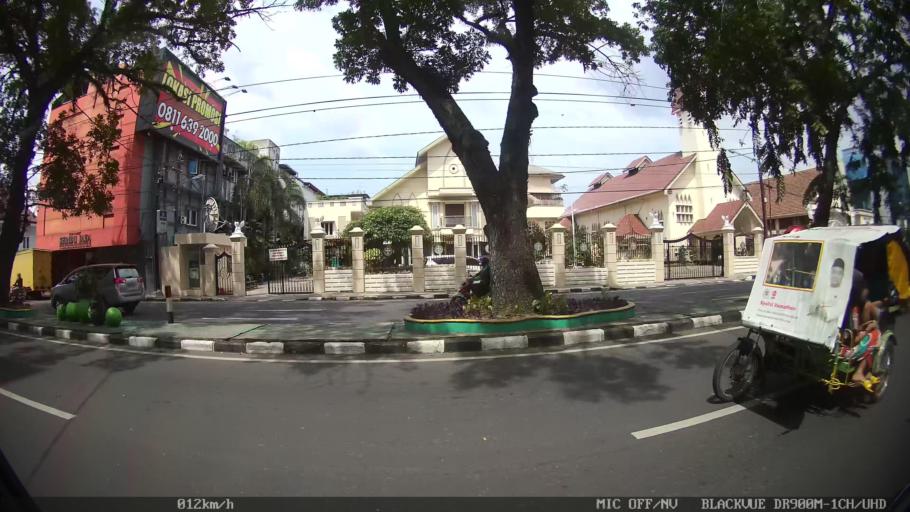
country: ID
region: North Sumatra
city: Medan
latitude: 3.5842
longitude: 98.6809
